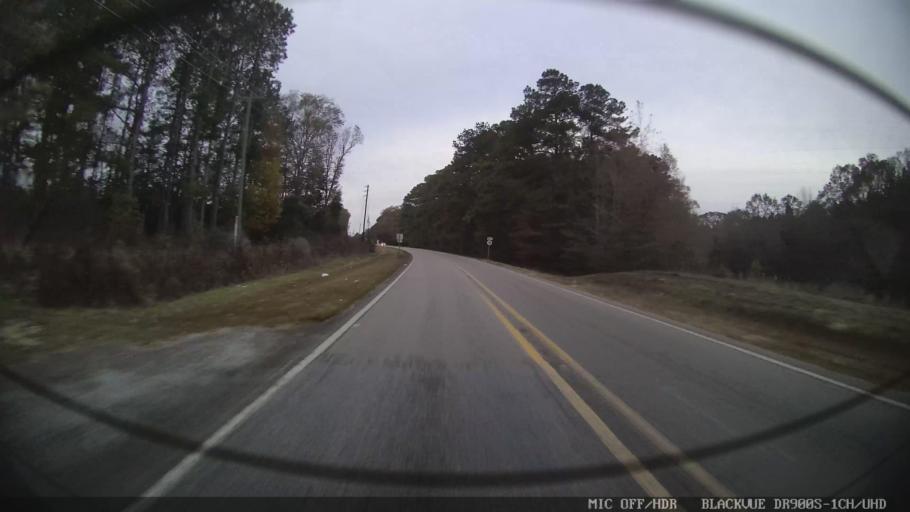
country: US
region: Mississippi
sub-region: Clarke County
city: Stonewall
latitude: 32.0231
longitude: -88.8524
